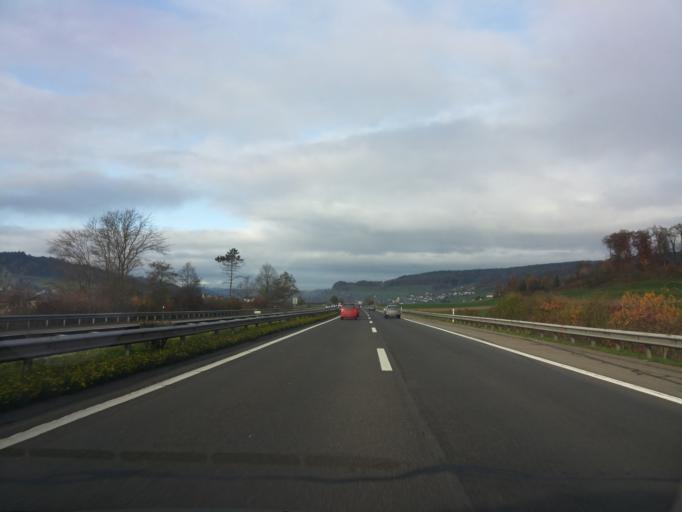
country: CH
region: Lucerne
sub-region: Sursee District
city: Knutwil
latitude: 47.2015
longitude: 8.0529
